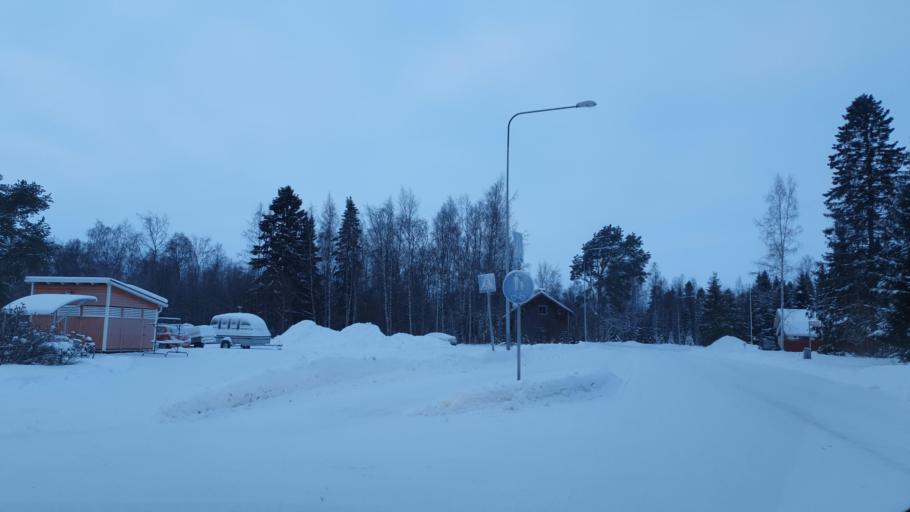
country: FI
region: Northern Ostrobothnia
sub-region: Oulu
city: Haukipudas
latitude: 65.2143
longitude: 25.3020
